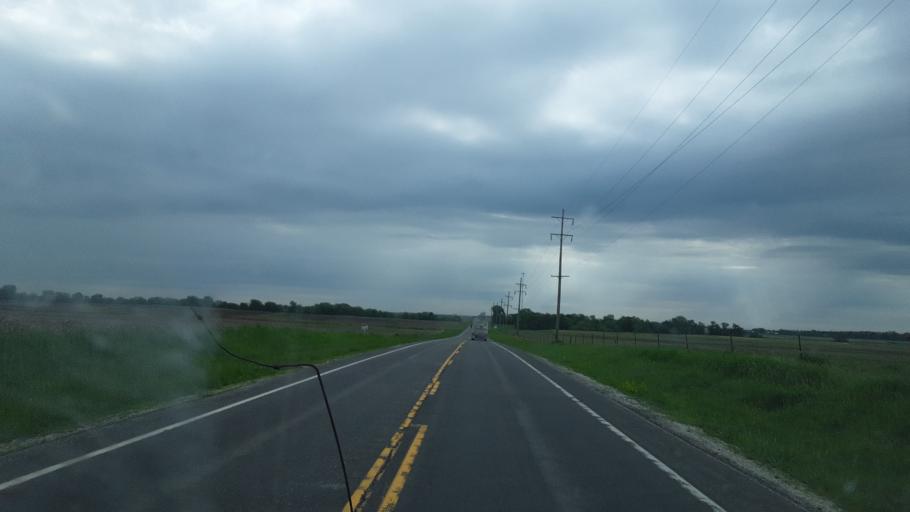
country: US
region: Illinois
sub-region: Fulton County
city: Astoria
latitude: 40.3567
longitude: -90.4050
